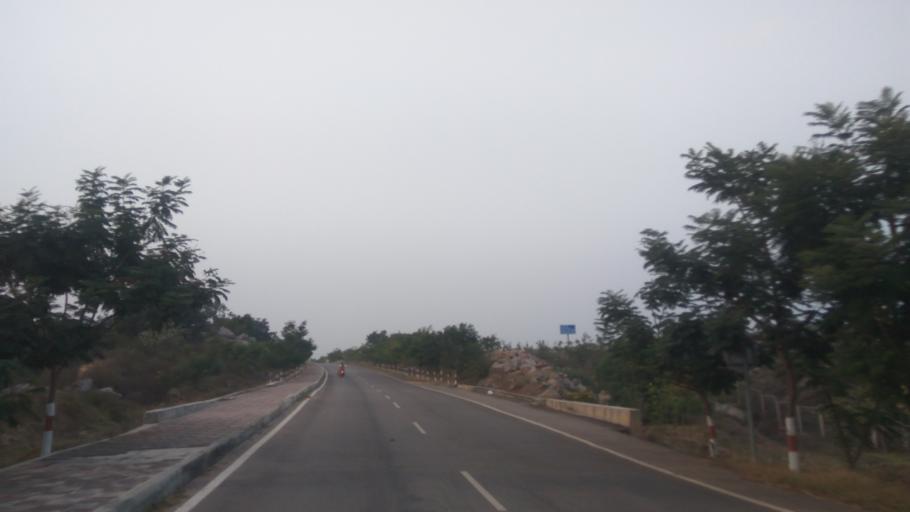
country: IN
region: Telangana
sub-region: Rangareddi
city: Secunderabad
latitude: 17.5596
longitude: 78.6260
